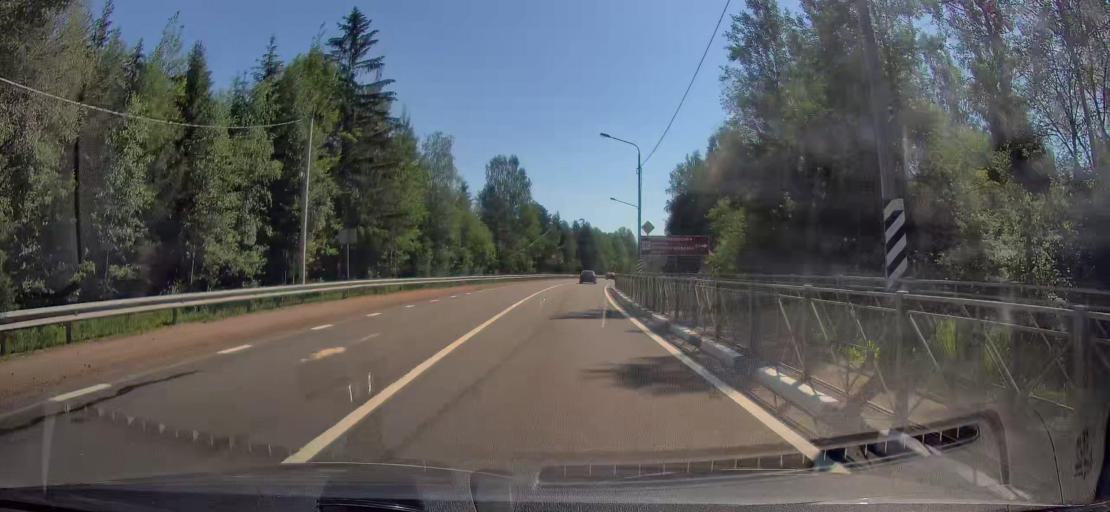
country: RU
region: Leningrad
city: Yefimovskiy
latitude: 59.3467
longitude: 34.8652
